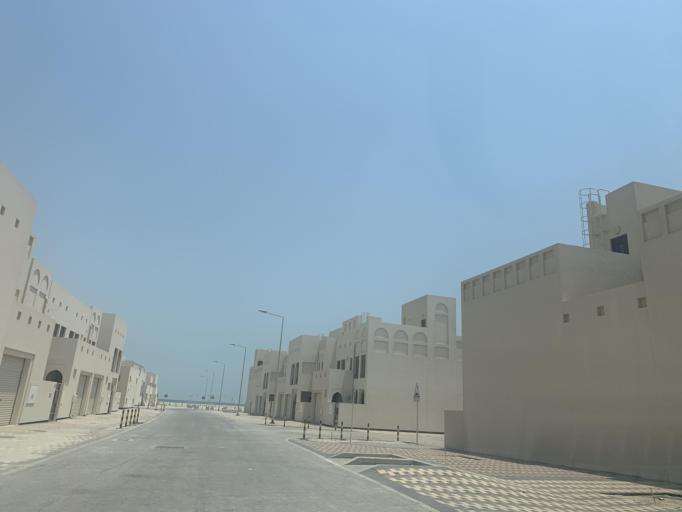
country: BH
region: Muharraq
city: Al Hadd
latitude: 26.2402
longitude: 50.6714
